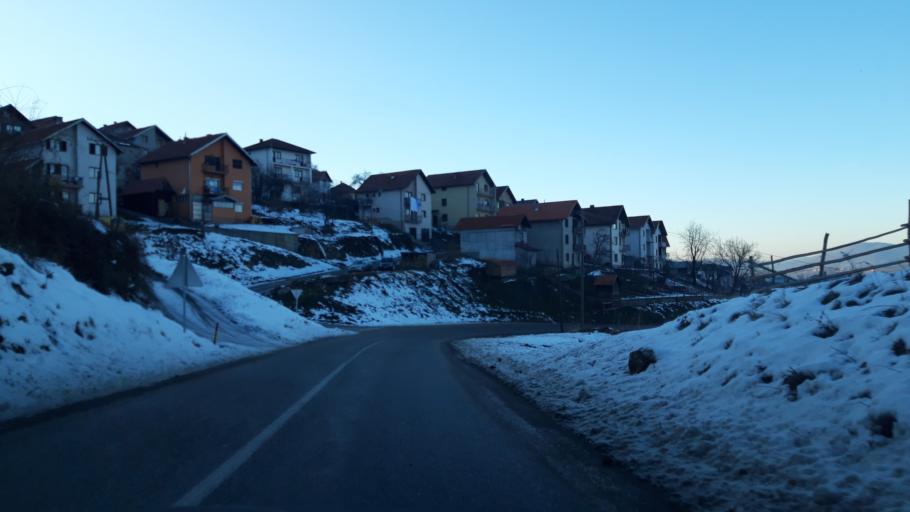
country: BA
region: Republika Srpska
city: Vlasenica
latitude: 44.1792
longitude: 18.9483
